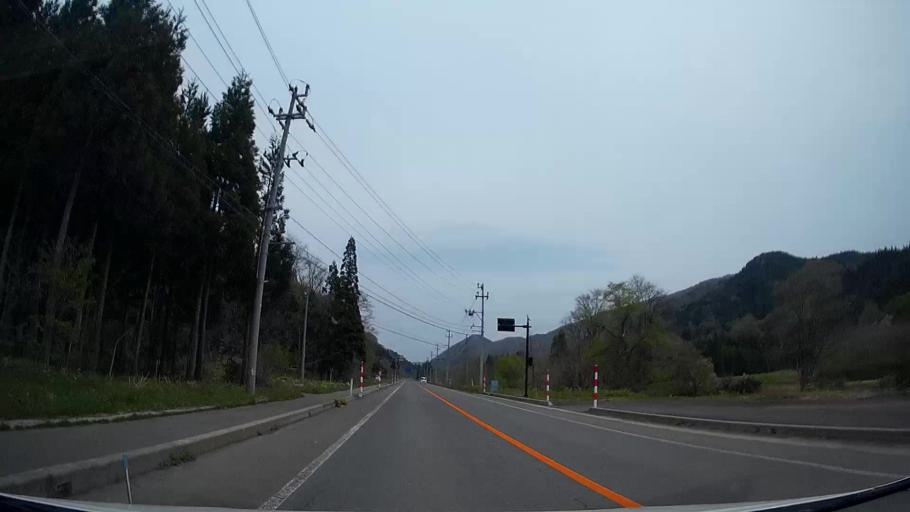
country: JP
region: Akita
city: Hanawa
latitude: 40.3377
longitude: 140.8282
